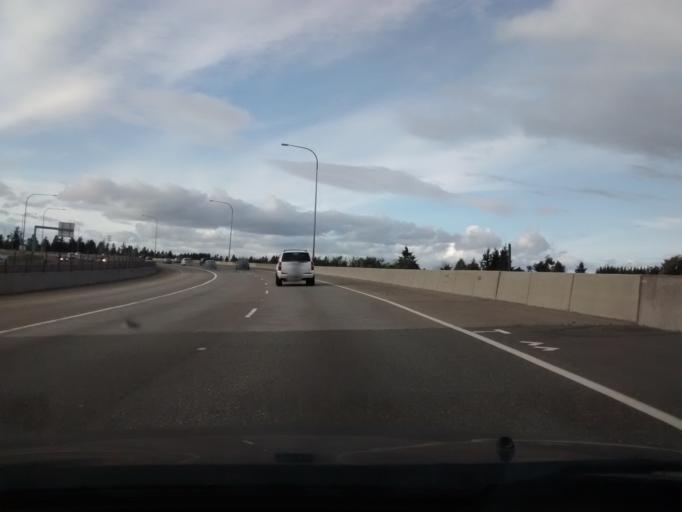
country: US
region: Washington
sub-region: Pierce County
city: Fircrest
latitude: 47.2549
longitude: -122.5136
